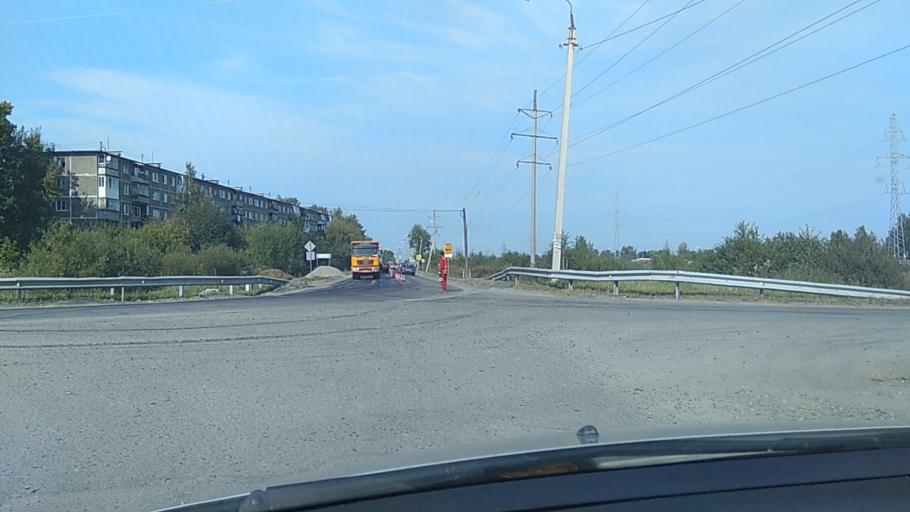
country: RU
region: Sverdlovsk
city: Sredneuralsk
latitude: 56.9790
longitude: 60.4754
